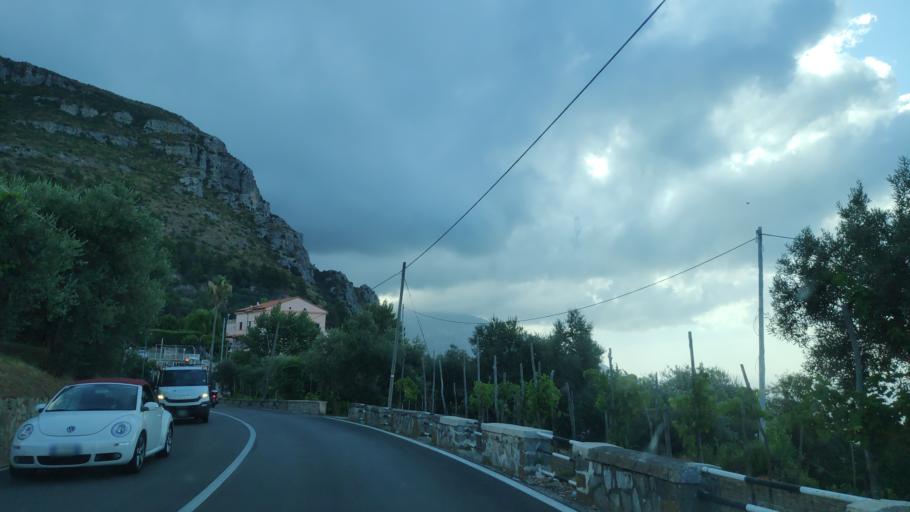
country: IT
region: Campania
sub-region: Provincia di Napoli
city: Arola-Preazzano
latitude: 40.6159
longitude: 14.4307
